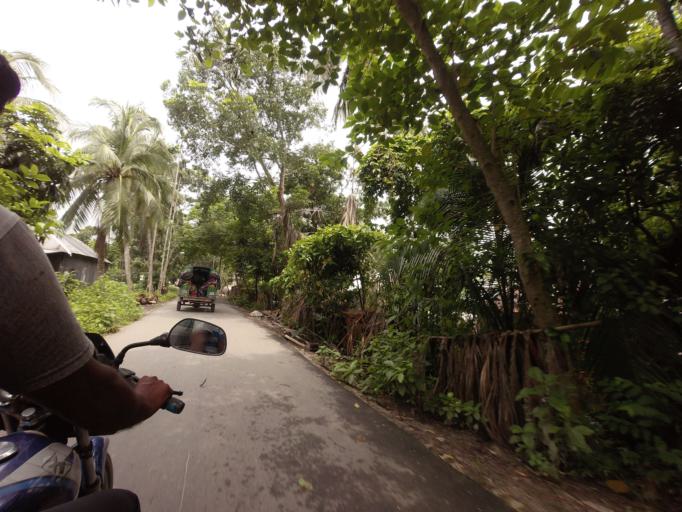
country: BD
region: Khulna
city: Kalia
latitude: 23.0864
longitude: 89.6672
